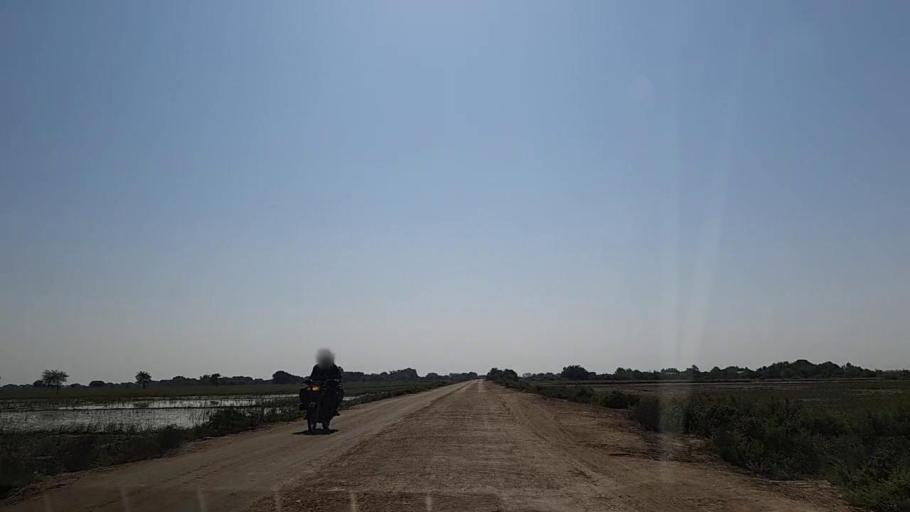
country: PK
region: Sindh
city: Chuhar Jamali
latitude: 24.5195
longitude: 68.0939
